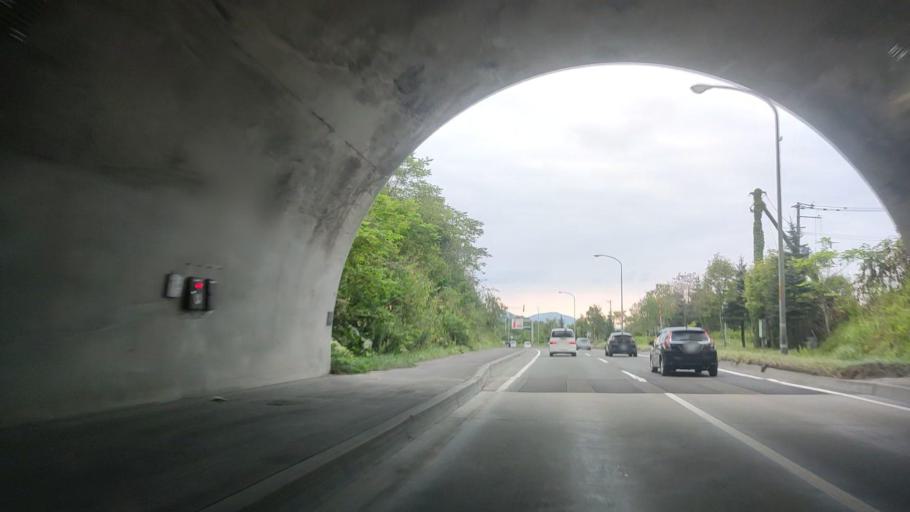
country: JP
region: Hokkaido
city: Otaru
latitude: 43.1667
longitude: 141.0932
